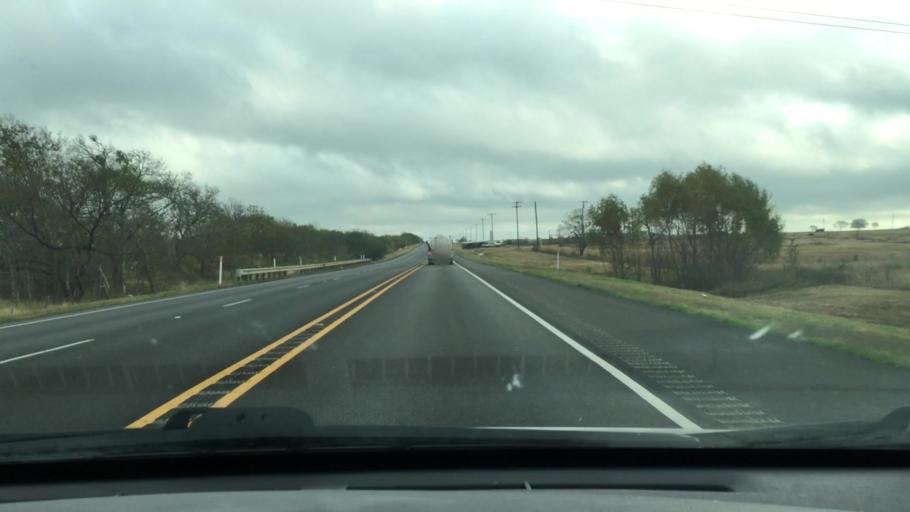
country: US
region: Texas
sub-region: Gonzales County
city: Nixon
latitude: 29.2581
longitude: -97.8052
